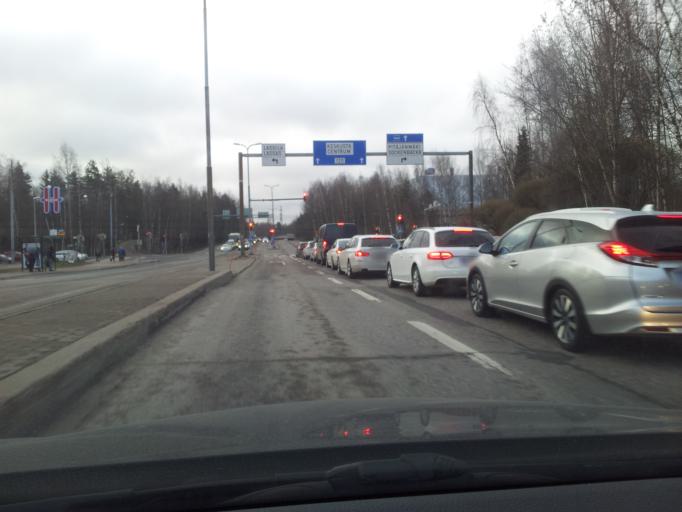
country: FI
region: Uusimaa
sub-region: Helsinki
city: Teekkarikylae
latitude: 60.2281
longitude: 24.8721
